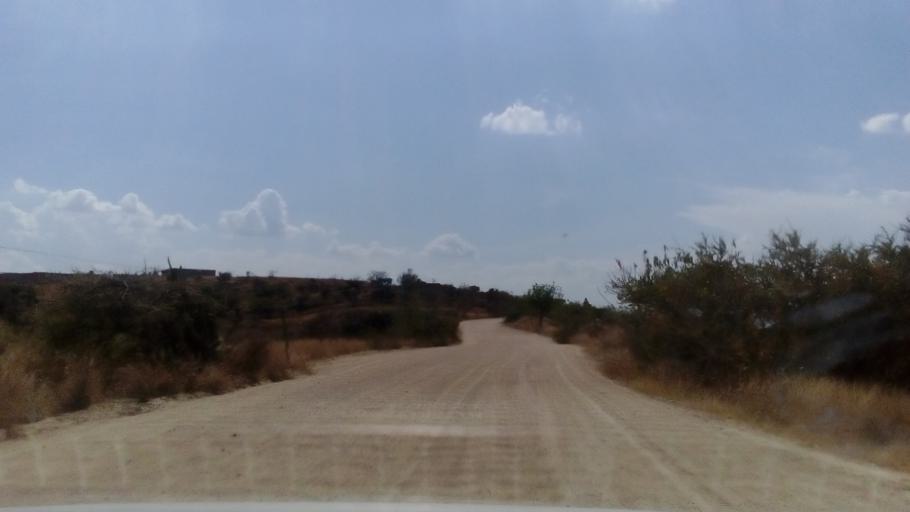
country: MX
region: Guanajuato
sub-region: Silao de la Victoria
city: Loma de Yerbabuena
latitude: 21.0871
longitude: -101.4430
